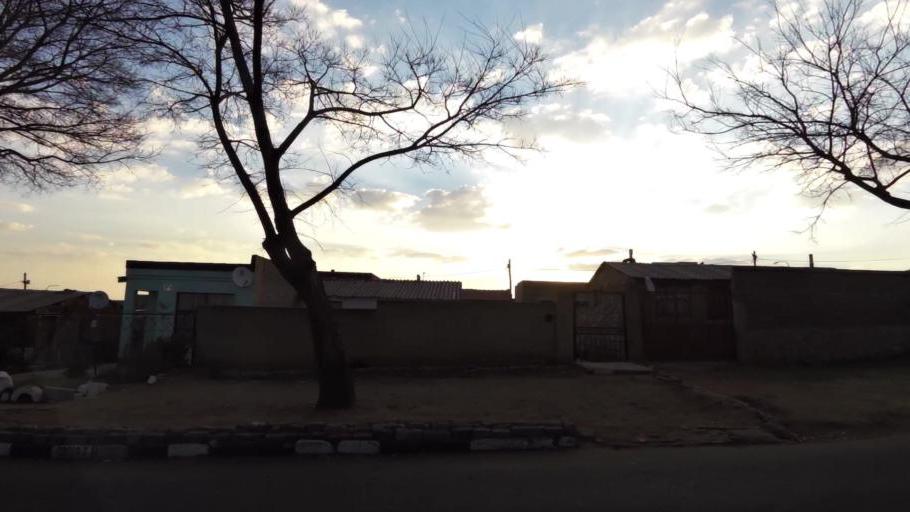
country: ZA
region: Gauteng
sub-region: City of Johannesburg Metropolitan Municipality
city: Soweto
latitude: -26.2193
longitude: 27.8923
